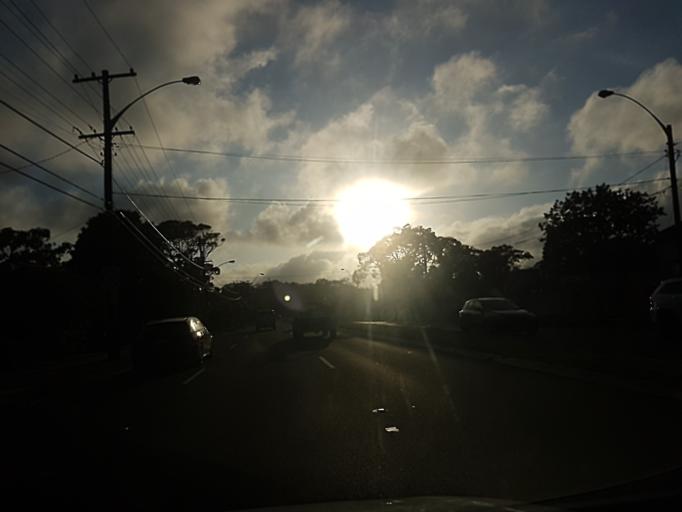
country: AU
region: New South Wales
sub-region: Warringah
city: Allambie Heights
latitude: -33.7530
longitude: 151.2562
